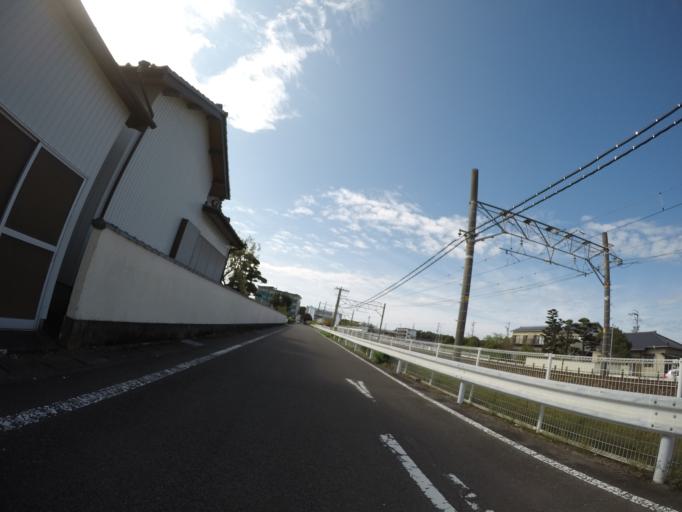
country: JP
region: Shizuoka
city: Fujieda
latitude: 34.8603
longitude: 138.2875
